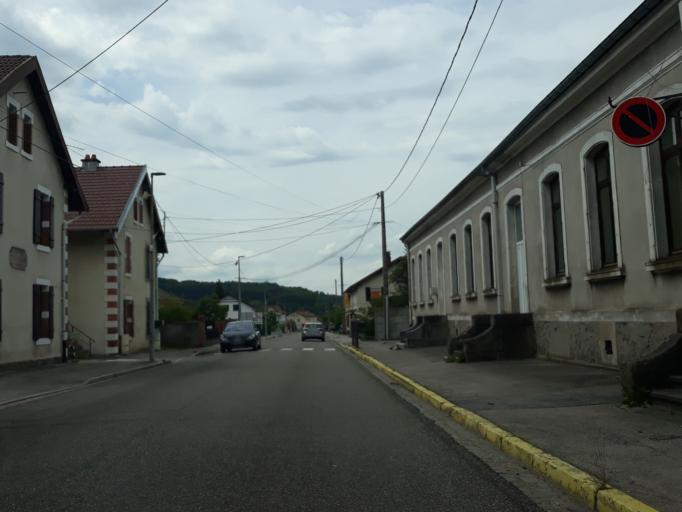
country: FR
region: Lorraine
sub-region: Departement des Vosges
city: Granges-sur-Vologne
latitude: 48.1458
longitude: 6.7876
